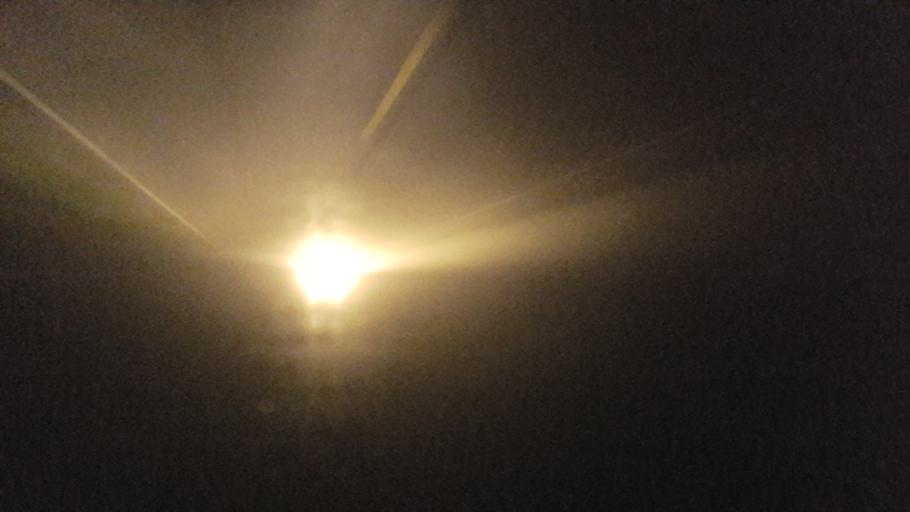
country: US
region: Ohio
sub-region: Knox County
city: Fredericktown
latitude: 40.5413
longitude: -82.4925
